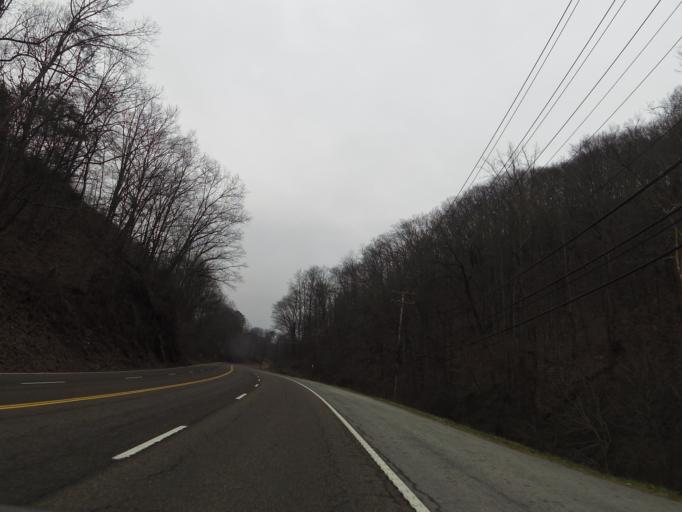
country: US
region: Tennessee
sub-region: Anderson County
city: Clinton
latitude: 36.0669
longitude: -84.1322
